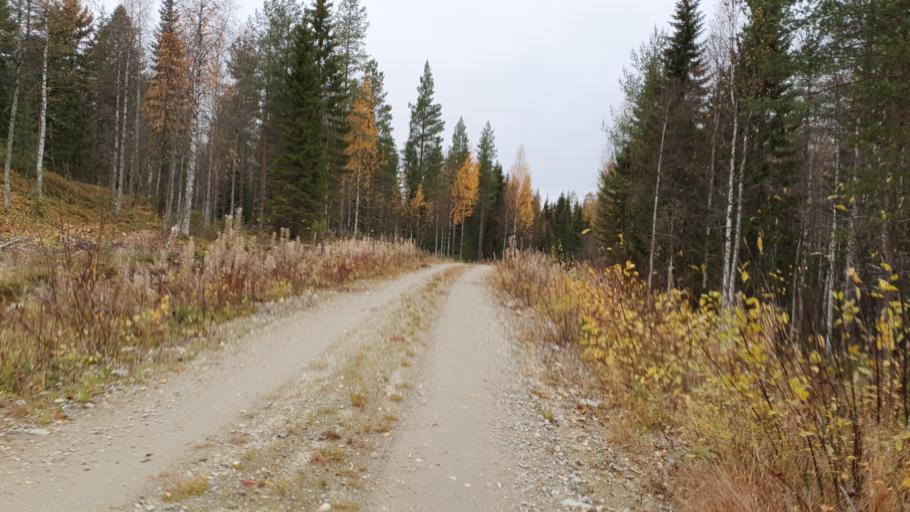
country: FI
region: Kainuu
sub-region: Kehys-Kainuu
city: Kuhmo
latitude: 64.4456
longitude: 29.6252
